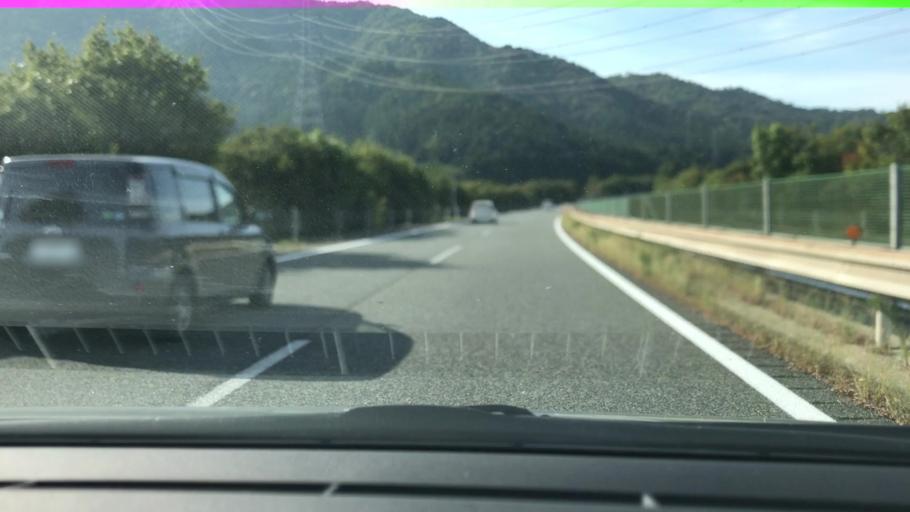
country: JP
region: Hyogo
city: Sasayama
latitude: 35.0379
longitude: 135.1827
